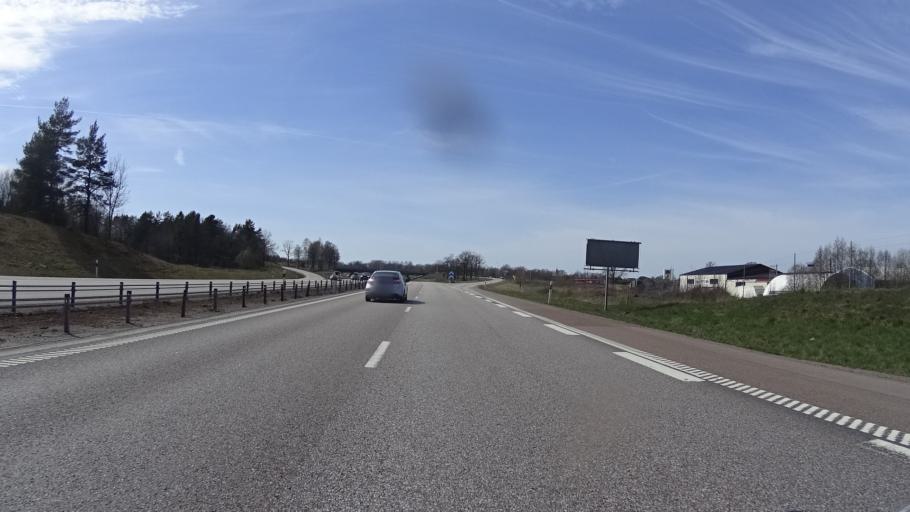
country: SE
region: OEstergoetland
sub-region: Odeshogs Kommun
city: OEdeshoeg
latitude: 58.2300
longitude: 14.6780
